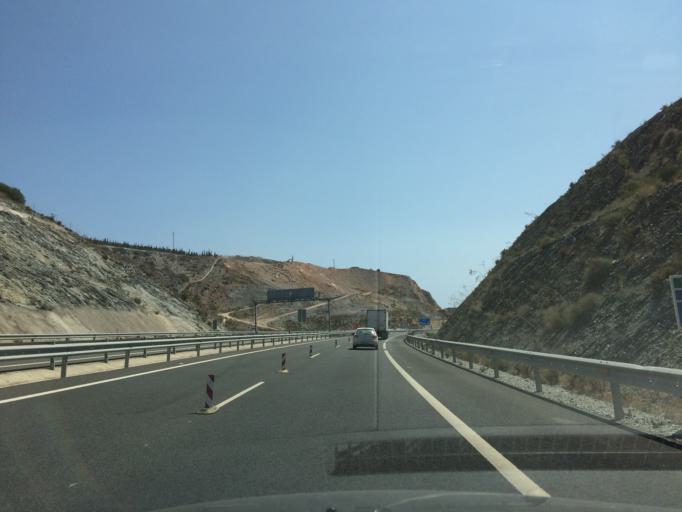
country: ES
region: Andalusia
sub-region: Provincia de Granada
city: Gualchos
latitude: 36.7185
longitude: -3.4282
